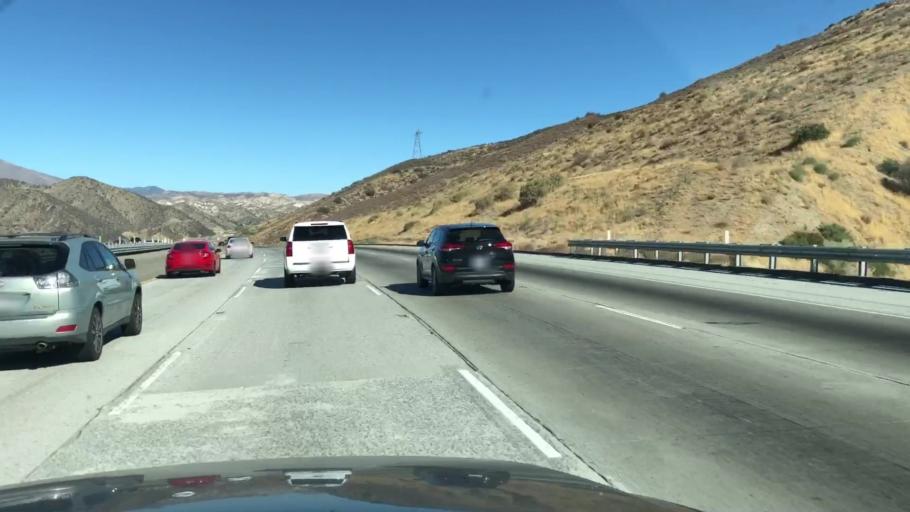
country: US
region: California
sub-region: Kern County
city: Lebec
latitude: 34.6807
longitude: -118.7790
